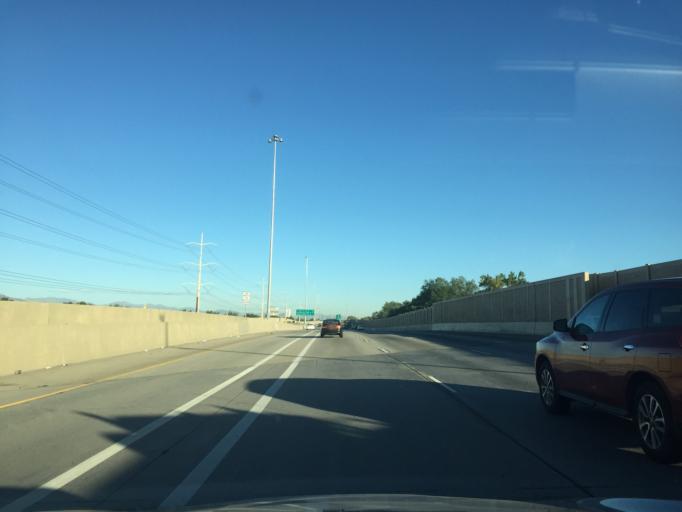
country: US
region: Utah
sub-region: Utah County
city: Provo
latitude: 40.2176
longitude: -111.6670
